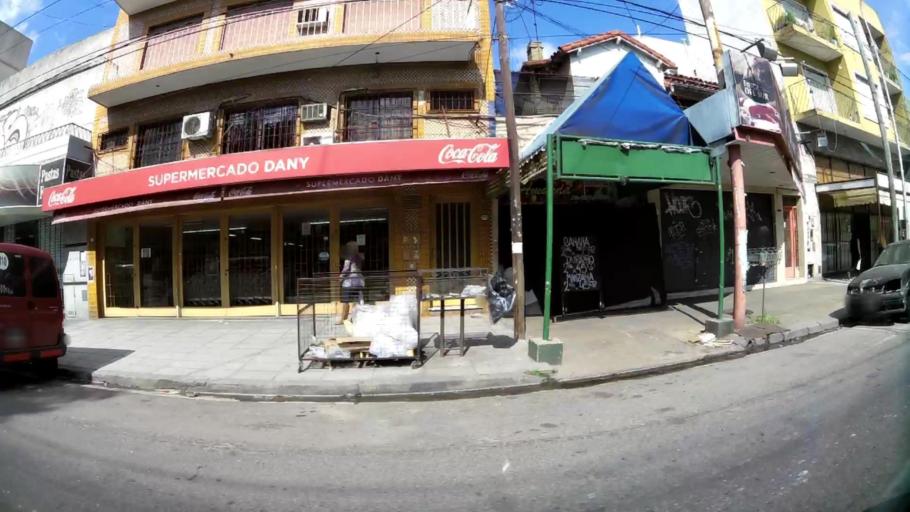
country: AR
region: Buenos Aires
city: San Justo
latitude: -34.6640
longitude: -58.5613
